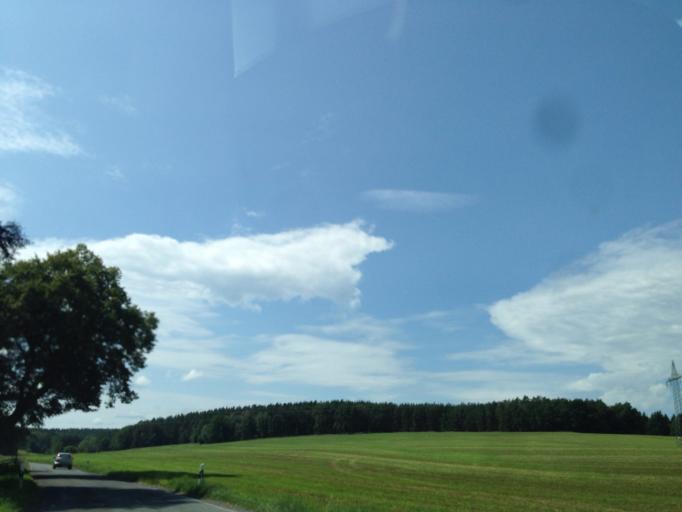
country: DE
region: Thuringia
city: Herschdorf
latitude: 50.7254
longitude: 11.5381
